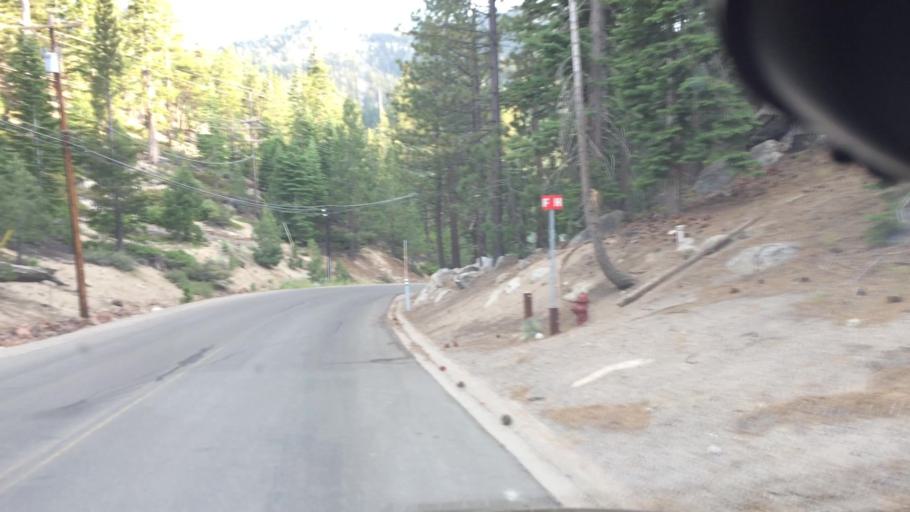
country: US
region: Nevada
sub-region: Douglas County
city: Kingsbury
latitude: 38.9698
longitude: -119.8892
